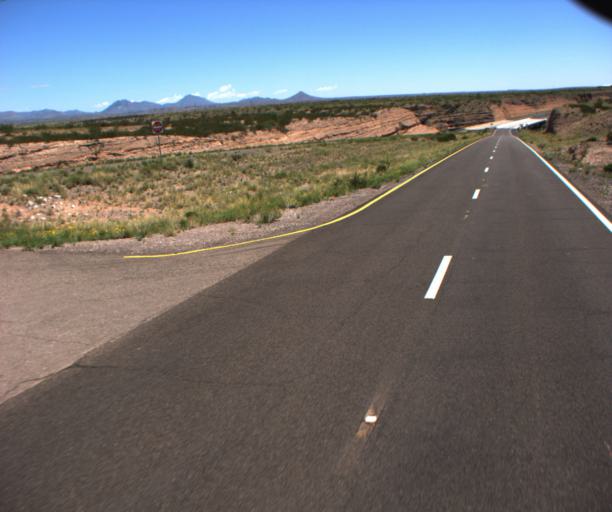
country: US
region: Arizona
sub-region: Greenlee County
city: Clifton
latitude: 32.9578
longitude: -109.2323
